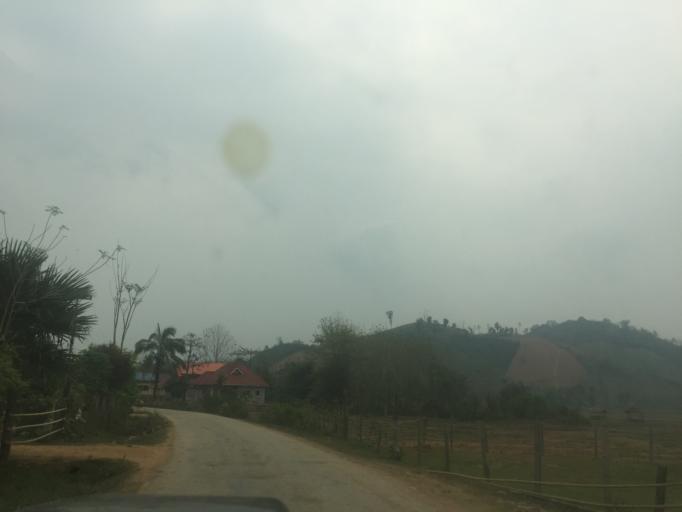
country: LA
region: Vientiane
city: Muang Sanakham
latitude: 18.3865
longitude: 101.5300
